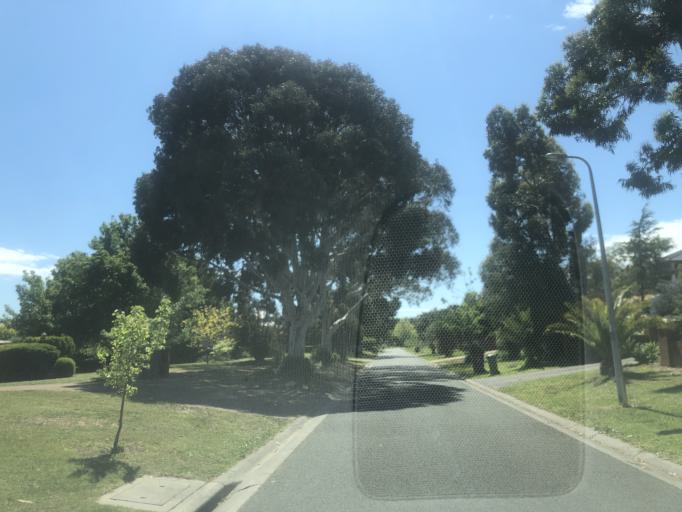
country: AU
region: Victoria
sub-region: Casey
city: Endeavour Hills
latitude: -37.9823
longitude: 145.2852
